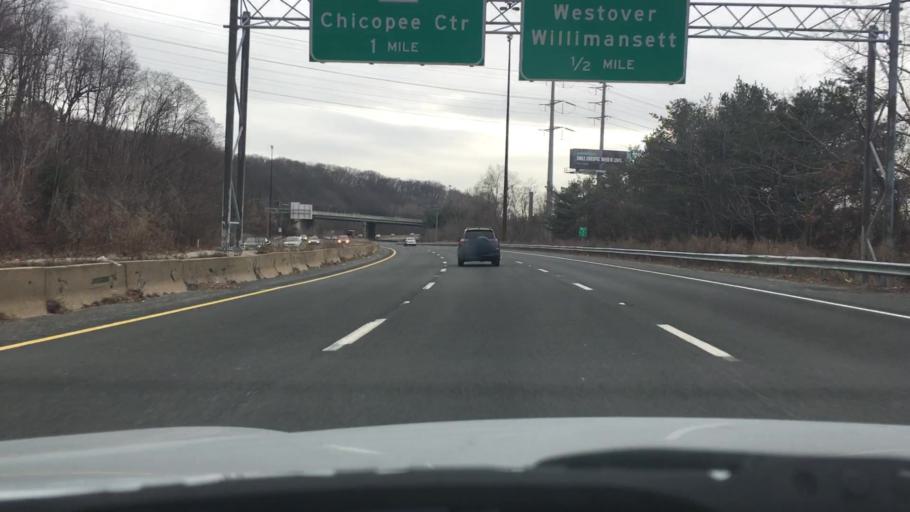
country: US
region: Massachusetts
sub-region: Hampden County
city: Chicopee
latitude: 42.1613
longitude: -72.6116
